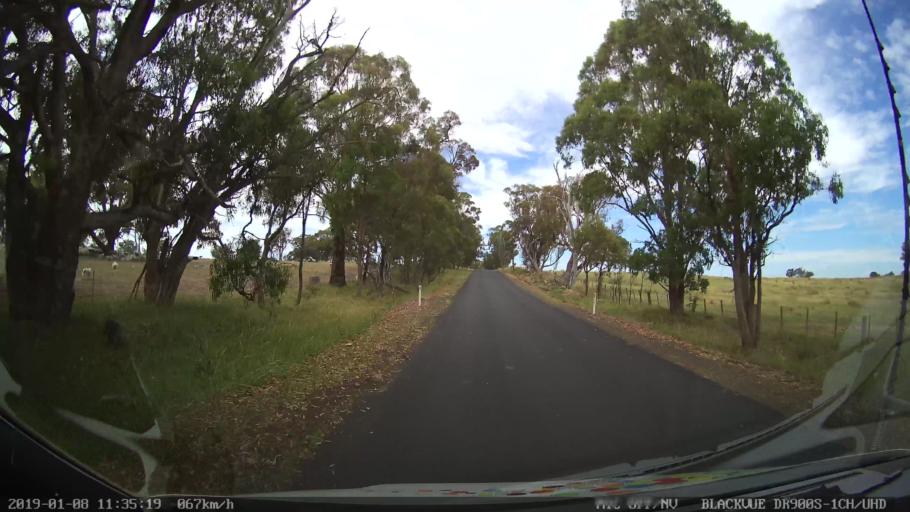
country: AU
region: New South Wales
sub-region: Guyra
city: Guyra
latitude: -30.3359
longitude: 151.5379
